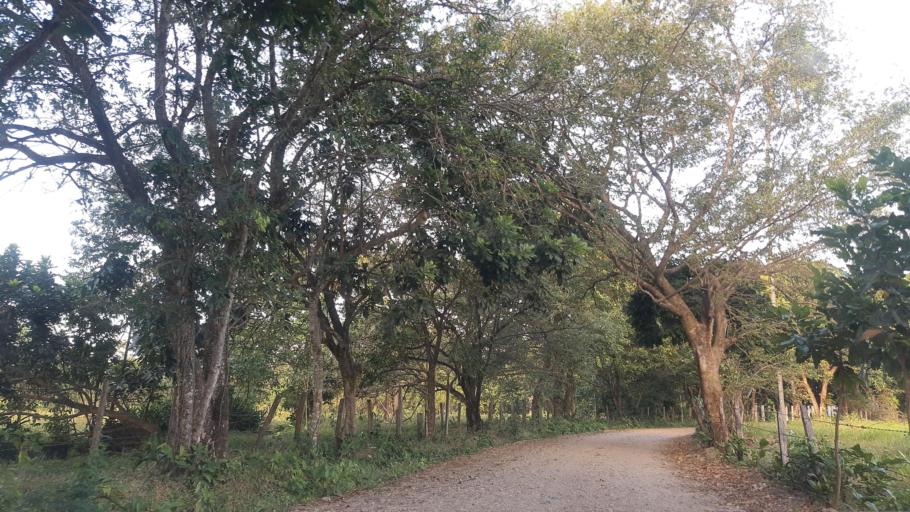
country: CO
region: Arauca
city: Tame
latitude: 6.4990
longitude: -71.7673
